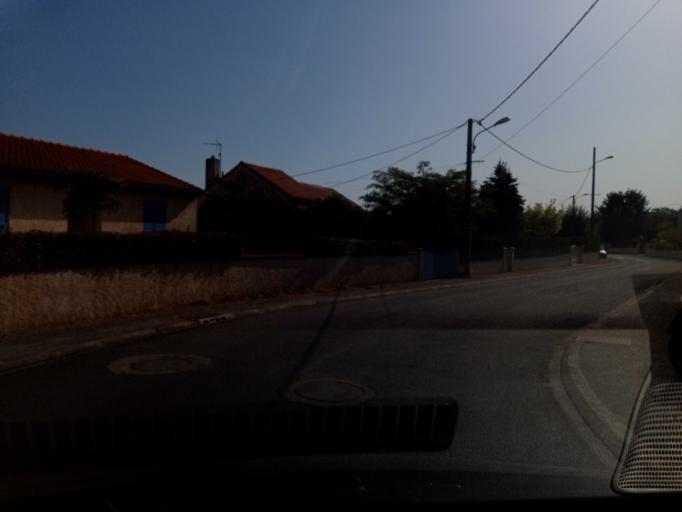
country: FR
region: Poitou-Charentes
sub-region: Departement de la Vienne
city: Saulge
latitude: 46.3752
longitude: 0.8800
